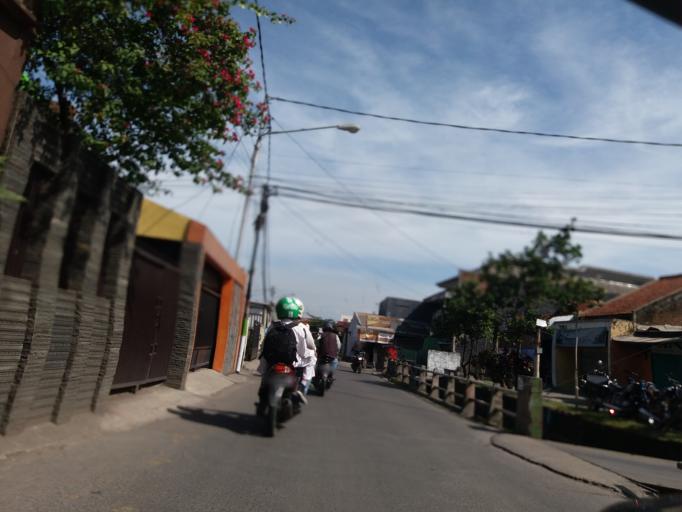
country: ID
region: West Java
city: Margahayukencana
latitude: -6.9453
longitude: 107.6024
